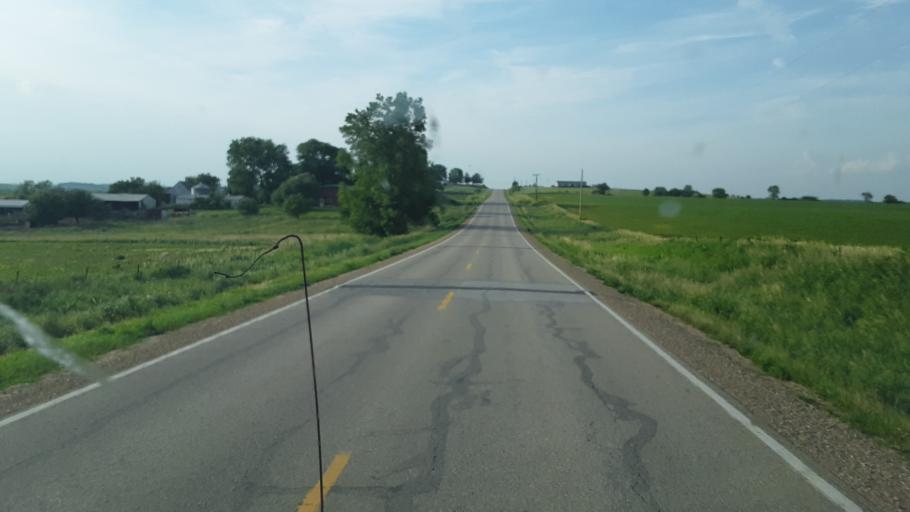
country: US
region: Iowa
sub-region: Tama County
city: Tama
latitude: 41.9666
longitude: -92.7085
